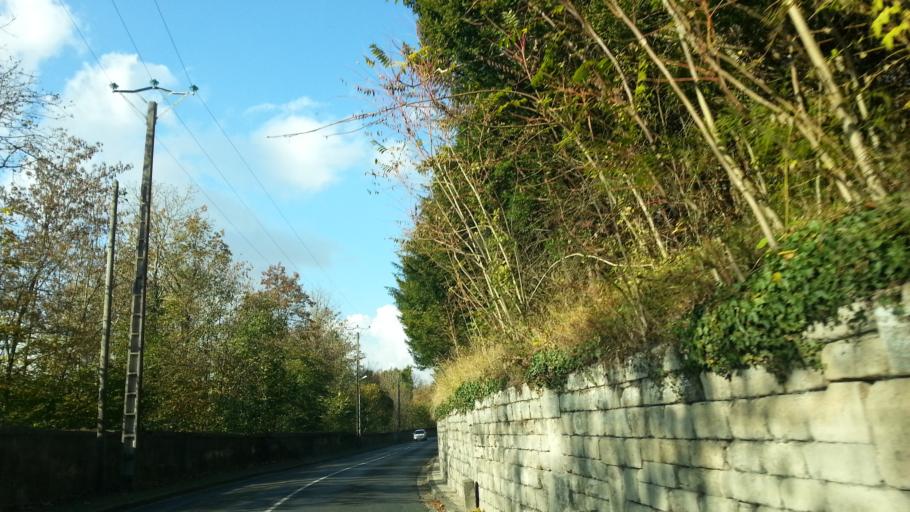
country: FR
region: Picardie
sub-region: Departement de l'Oise
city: Cires-les-Mello
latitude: 49.2677
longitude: 2.3672
